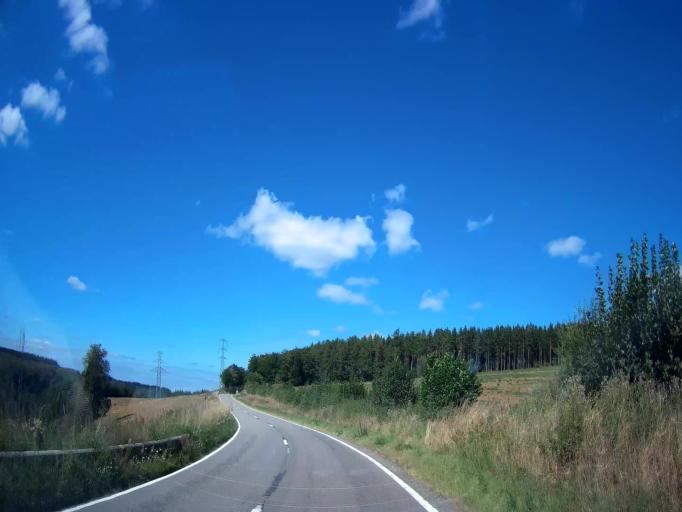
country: BE
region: Wallonia
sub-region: Province du Luxembourg
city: La Roche-en-Ardenne
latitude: 50.1586
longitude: 5.6078
